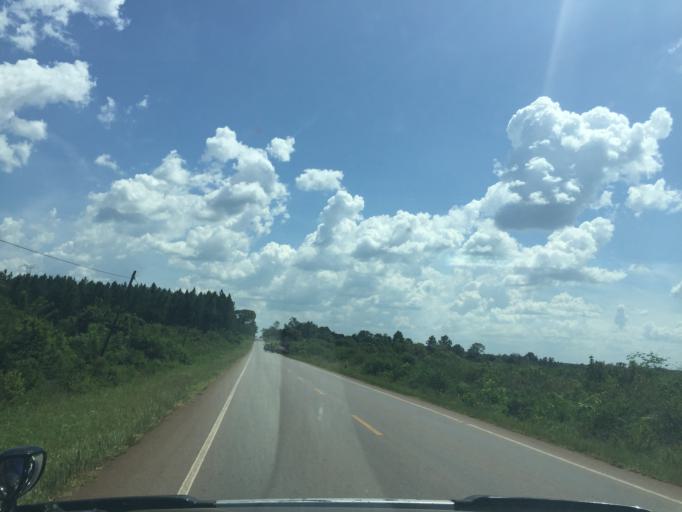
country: UG
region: Central Region
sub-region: Nakasongola District
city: Nakasongola
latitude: 1.2059
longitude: 32.4635
